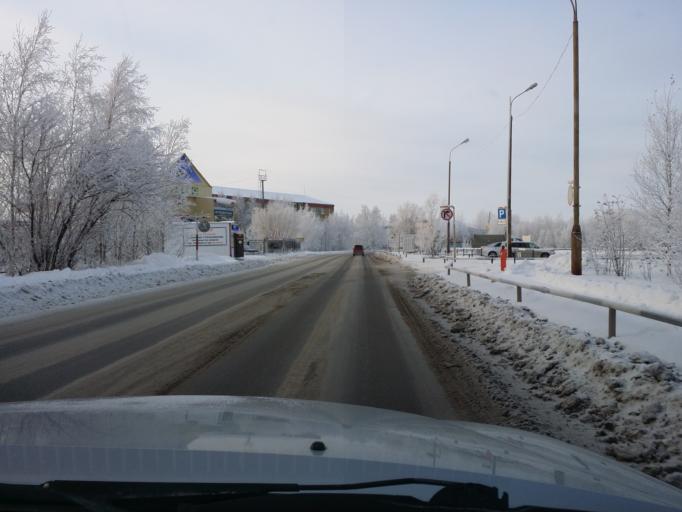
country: RU
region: Khanty-Mansiyskiy Avtonomnyy Okrug
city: Nizhnevartovsk
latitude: 60.9398
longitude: 76.5286
